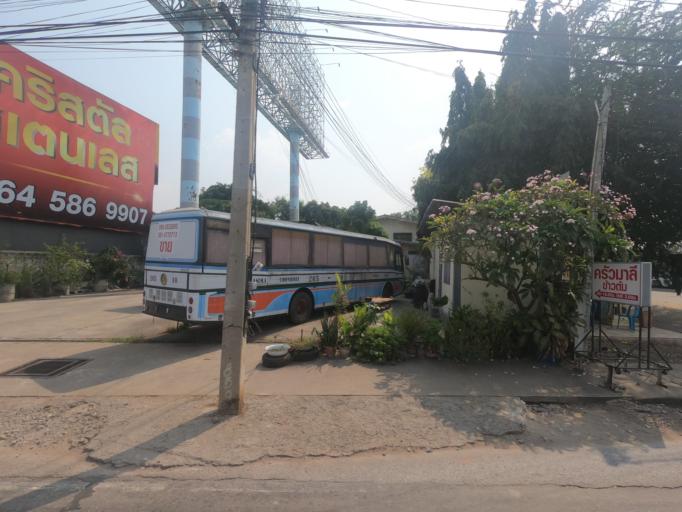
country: TH
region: Nakhon Ratchasima
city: Nakhon Ratchasima
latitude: 14.9598
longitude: 102.0571
